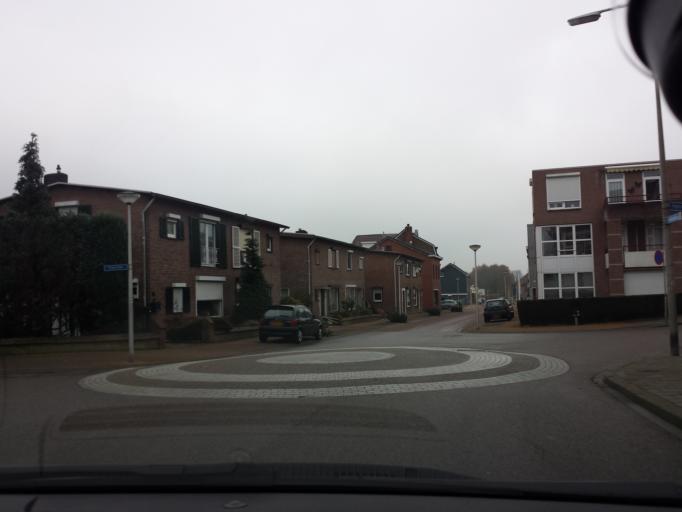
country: NL
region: Limburg
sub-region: Gemeente Kerkrade
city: Kerkrade
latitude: 50.8602
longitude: 6.0661
